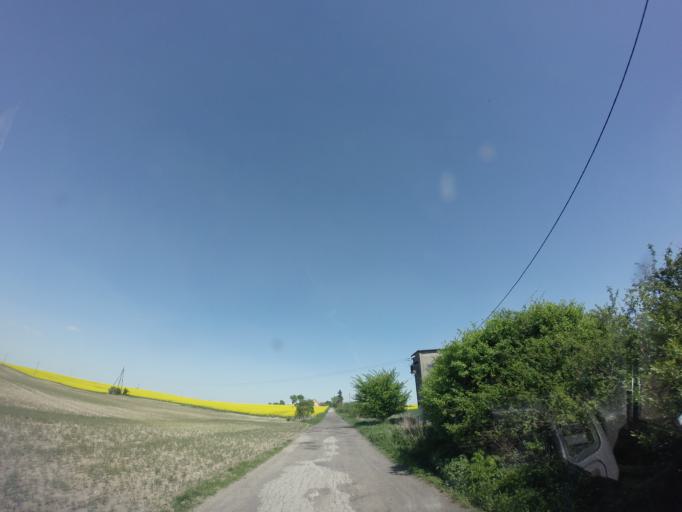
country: PL
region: West Pomeranian Voivodeship
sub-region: Powiat choszczenski
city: Pelczyce
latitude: 53.0167
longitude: 15.3411
